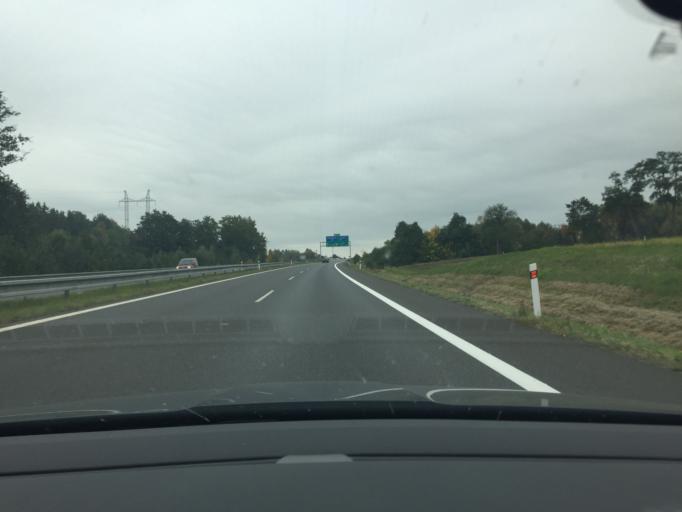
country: CZ
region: Jihocesky
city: Mirotice
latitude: 49.3627
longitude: 14.0553
